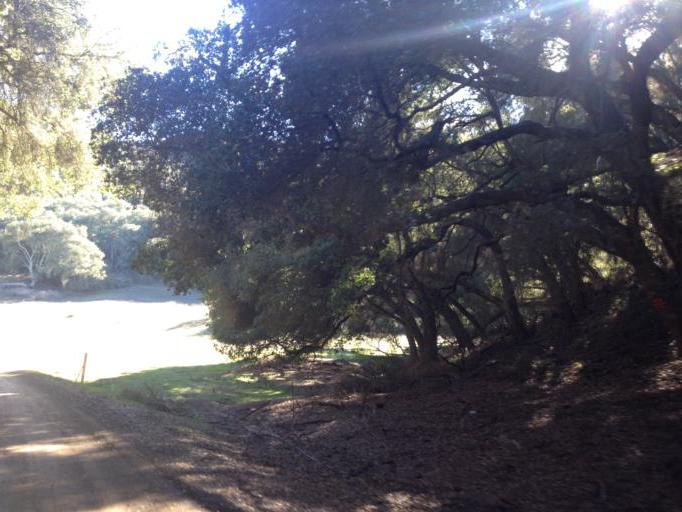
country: US
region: California
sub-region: San Luis Obispo County
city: Avila Beach
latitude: 35.2405
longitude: -120.7752
